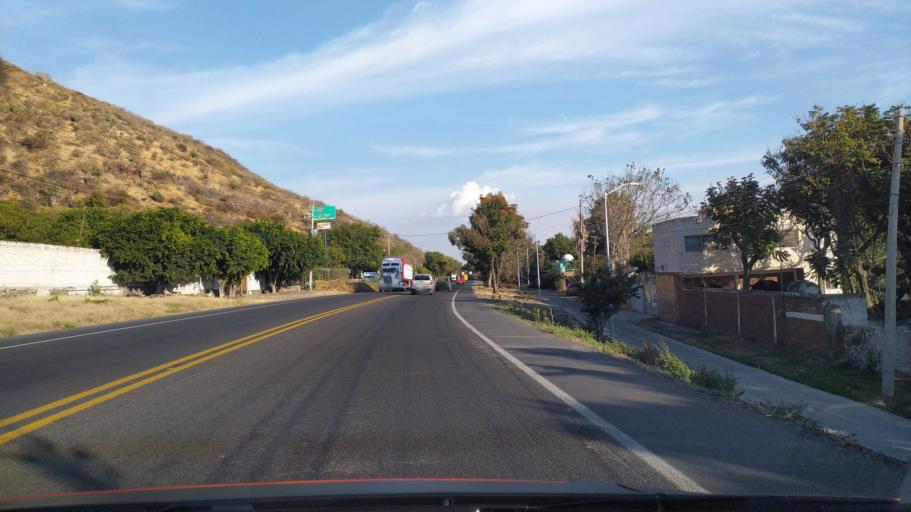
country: MX
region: Jalisco
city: Jamay
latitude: 20.2944
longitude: -102.7361
